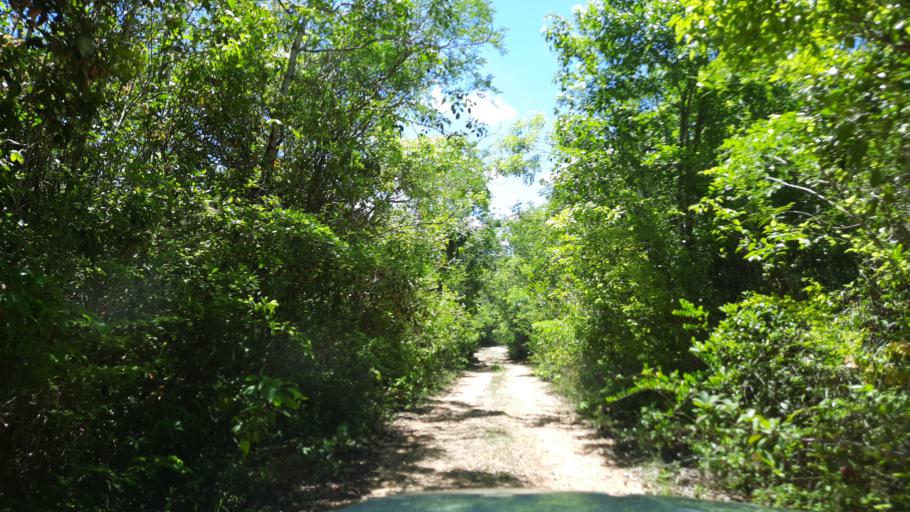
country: BZ
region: Cayo
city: Belmopan
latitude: 17.3560
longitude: -88.5431
